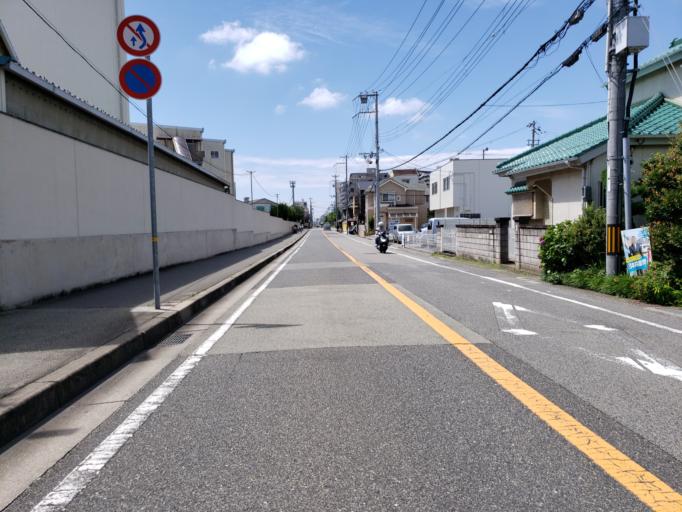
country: JP
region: Hyogo
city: Kakogawacho-honmachi
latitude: 34.7158
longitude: 134.8900
